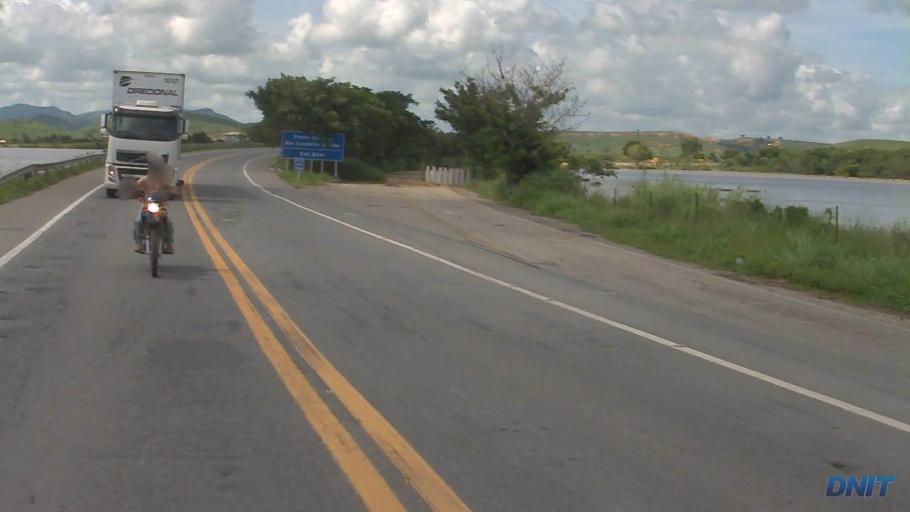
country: BR
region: Minas Gerais
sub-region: Governador Valadares
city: Governador Valadares
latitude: -19.0459
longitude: -42.1534
